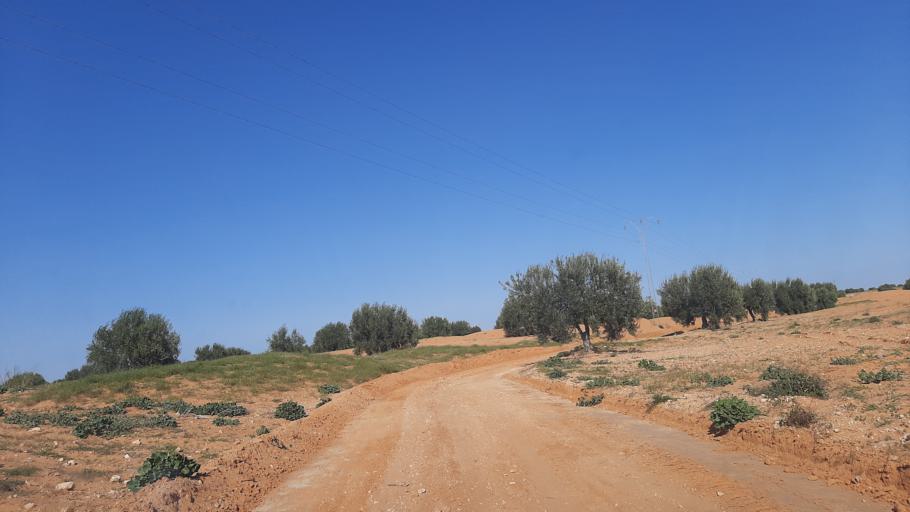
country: TN
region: Madanin
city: Medenine
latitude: 33.2824
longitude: 10.7832
